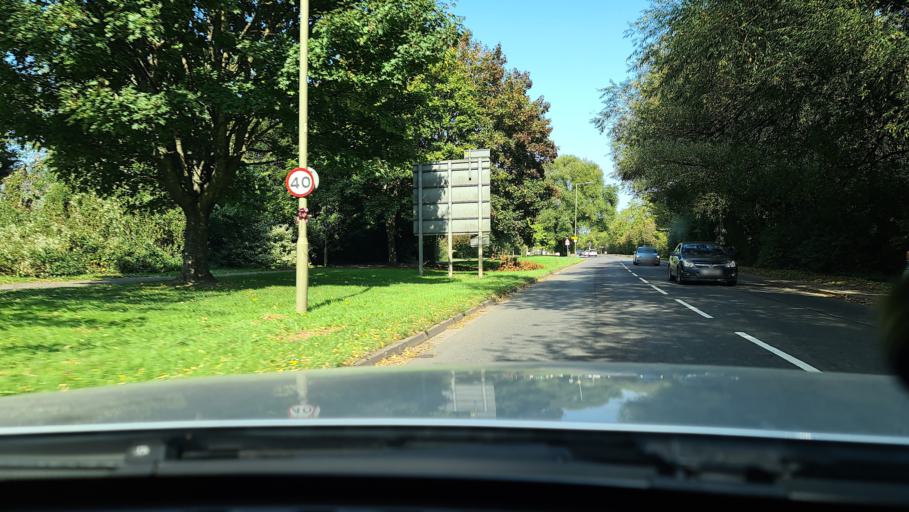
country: GB
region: England
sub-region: Oxfordshire
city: Banbury
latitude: 52.0740
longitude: -1.3370
